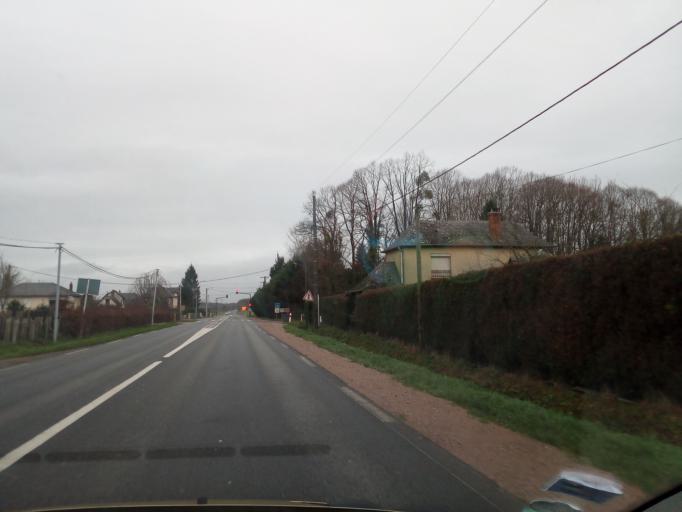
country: FR
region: Haute-Normandie
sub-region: Departement de l'Eure
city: Hauville
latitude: 49.4019
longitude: 0.7974
